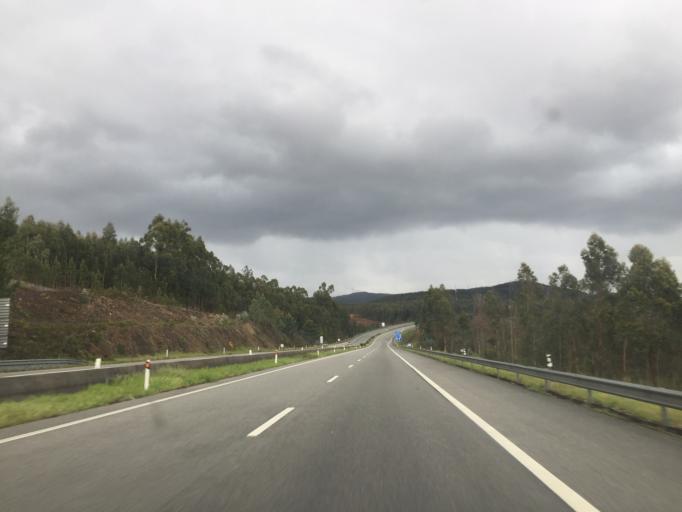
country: PT
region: Aveiro
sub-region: Agueda
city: Valongo
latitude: 40.6673
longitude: -8.4044
